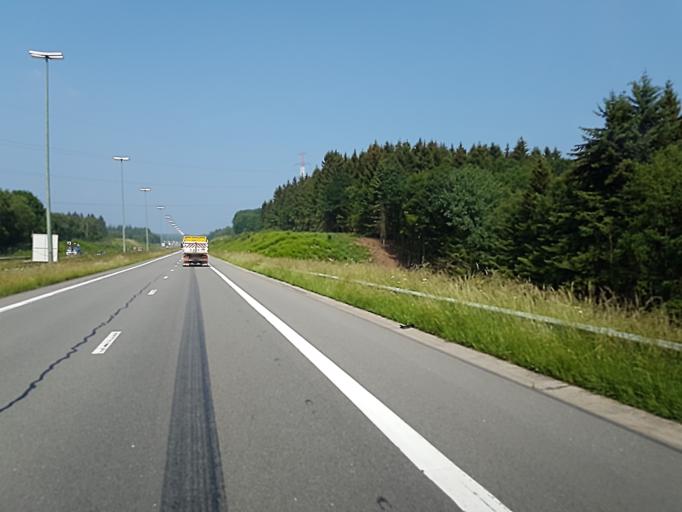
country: BE
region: Wallonia
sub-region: Province de Liege
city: Ferrieres
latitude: 50.3892
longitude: 5.6849
